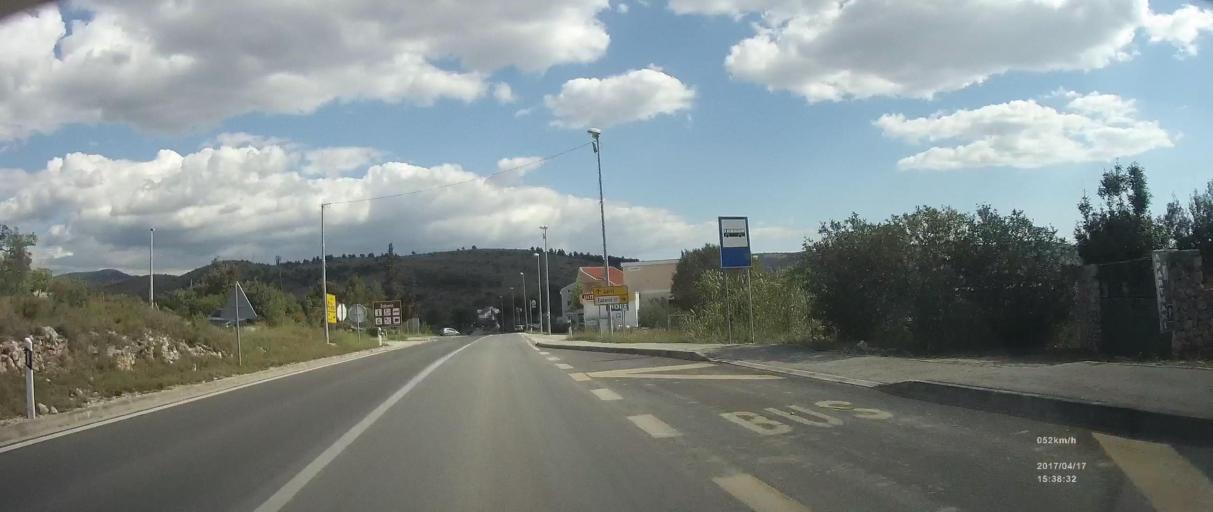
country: HR
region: Sibensko-Kniniska
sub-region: Grad Sibenik
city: Brodarica
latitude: 43.6635
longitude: 15.9443
